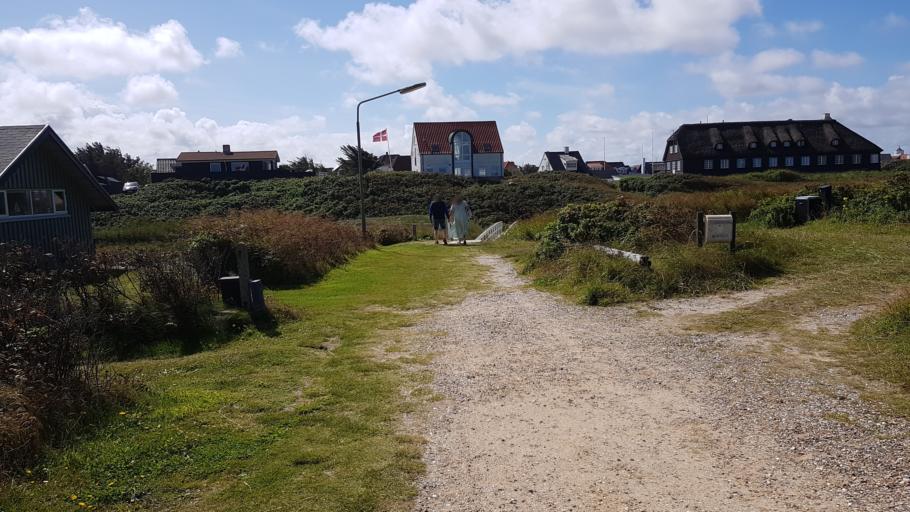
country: DK
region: North Denmark
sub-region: Jammerbugt Kommune
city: Pandrup
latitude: 57.3764
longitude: 9.7171
